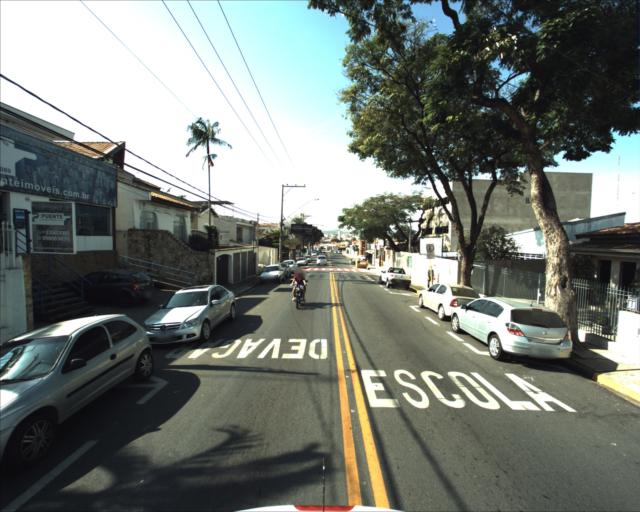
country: BR
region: Sao Paulo
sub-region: Sorocaba
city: Sorocaba
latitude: -23.4911
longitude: -47.4521
